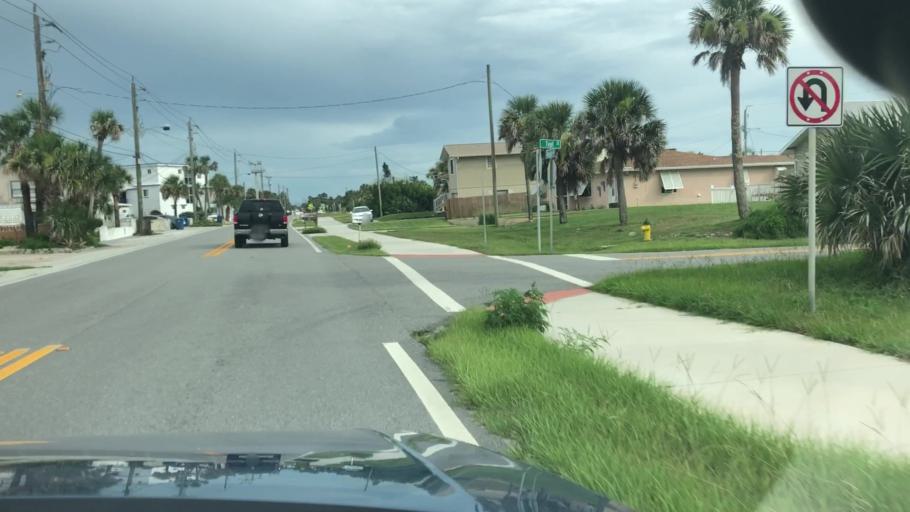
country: US
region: Florida
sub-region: Volusia County
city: Port Orange
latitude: 29.1347
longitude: -80.9597
